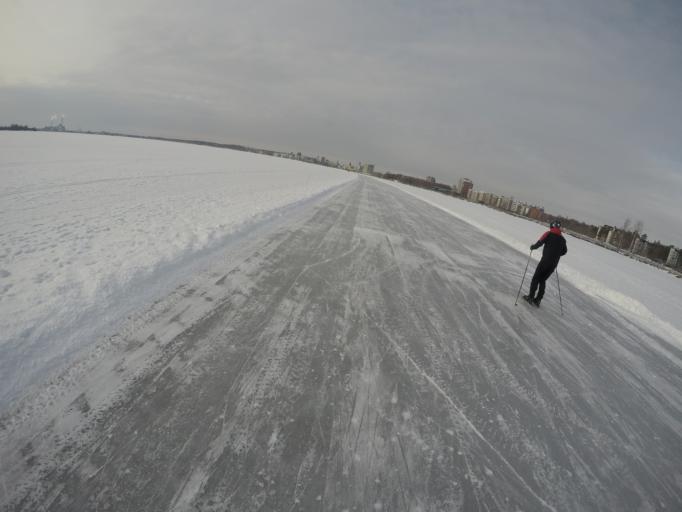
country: SE
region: Vaestmanland
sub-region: Vasteras
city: Vasteras
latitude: 59.5955
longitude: 16.5828
